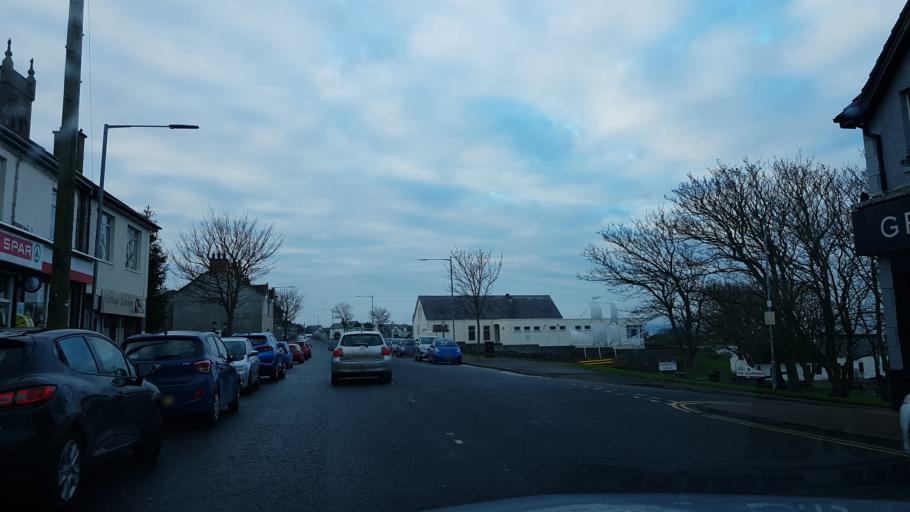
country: GB
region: Northern Ireland
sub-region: North Down District
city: Bangor
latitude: 54.6756
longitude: -5.6171
